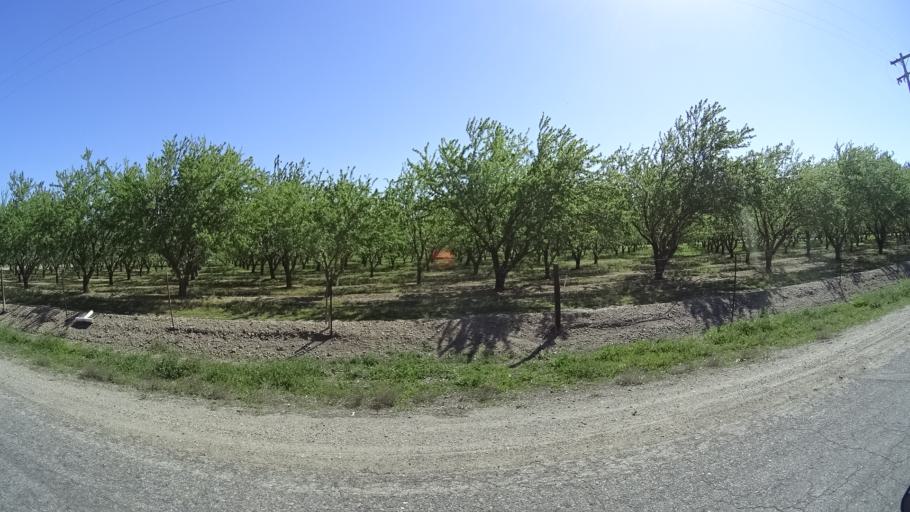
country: US
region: California
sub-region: Glenn County
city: Orland
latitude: 39.7124
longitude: -122.2113
